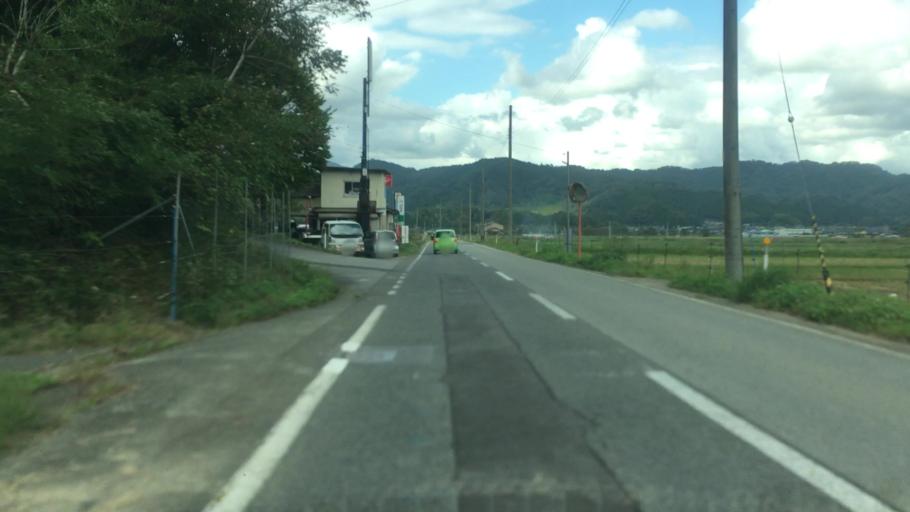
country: JP
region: Hyogo
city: Toyooka
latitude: 35.4463
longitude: 134.7298
